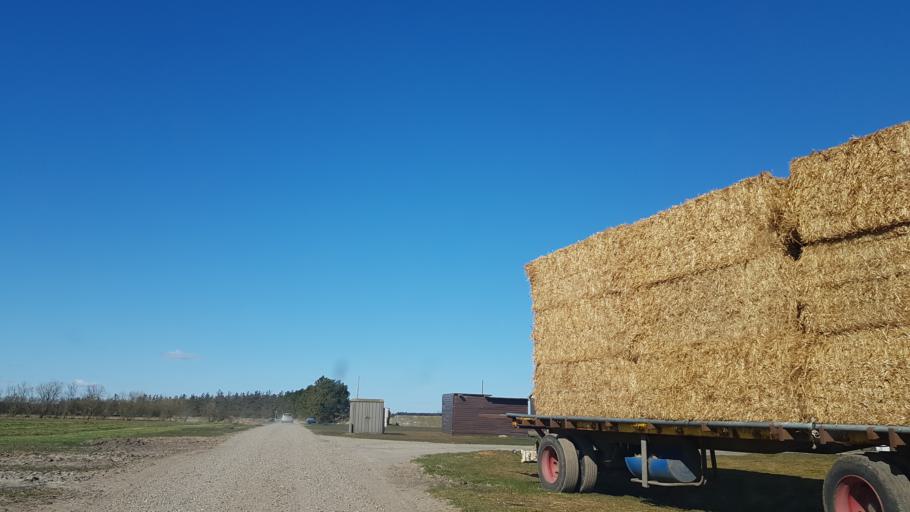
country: DK
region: South Denmark
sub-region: Tonder Kommune
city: Sherrebek
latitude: 55.2428
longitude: 8.7136
